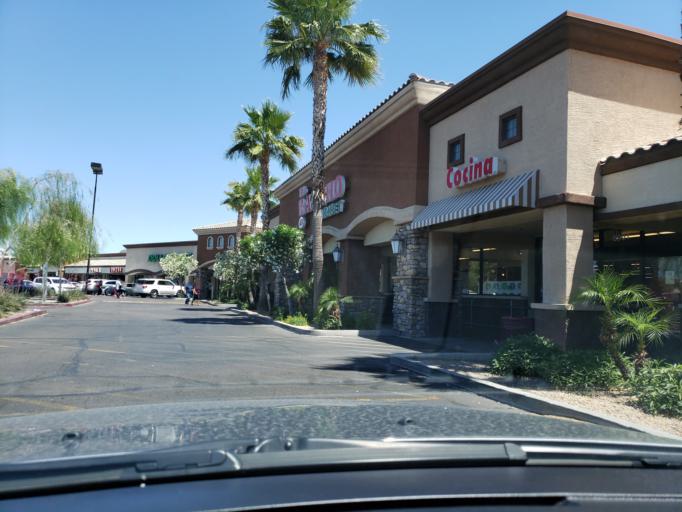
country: US
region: Arizona
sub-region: Maricopa County
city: Glendale
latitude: 33.5662
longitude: -112.0986
